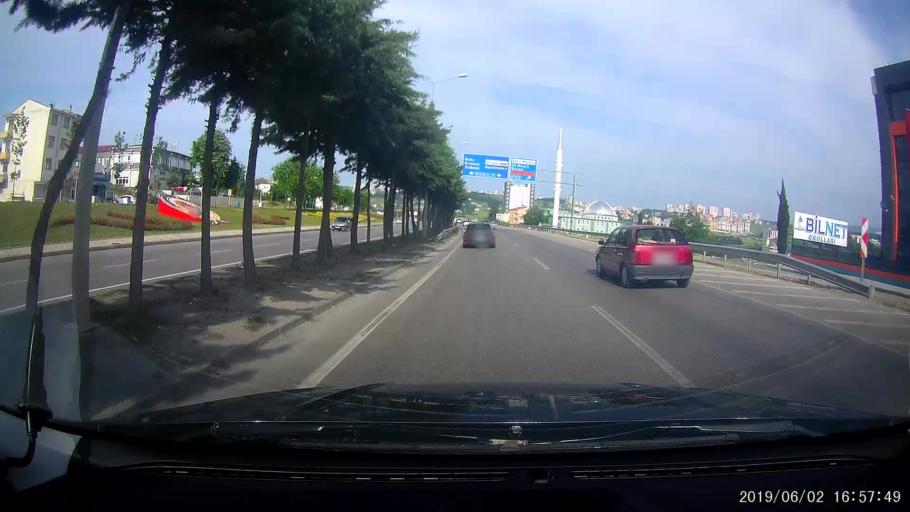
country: TR
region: Samsun
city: Samsun
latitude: 41.2902
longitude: 36.2792
